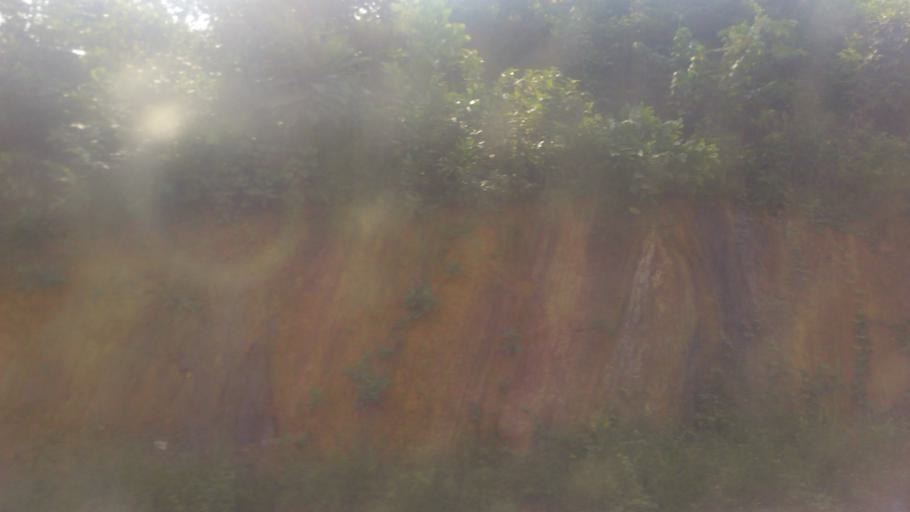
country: CI
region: Sud-Comoe
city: Tiapoum
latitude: 5.2786
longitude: -2.8003
